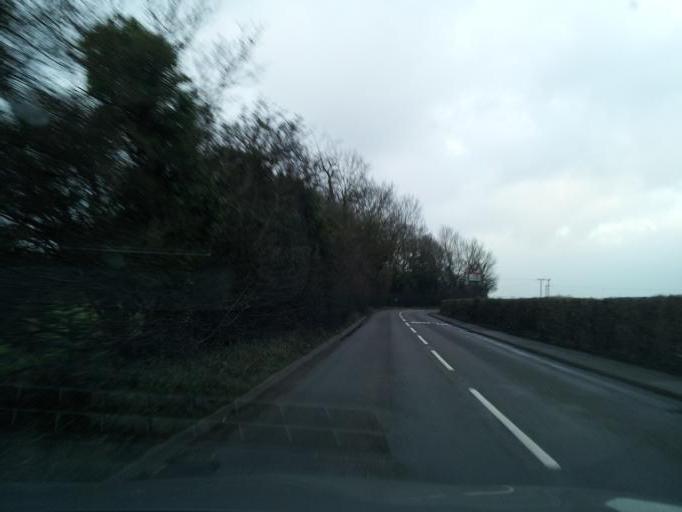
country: GB
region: England
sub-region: Derbyshire
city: Etwall
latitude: 52.8619
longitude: -1.6136
